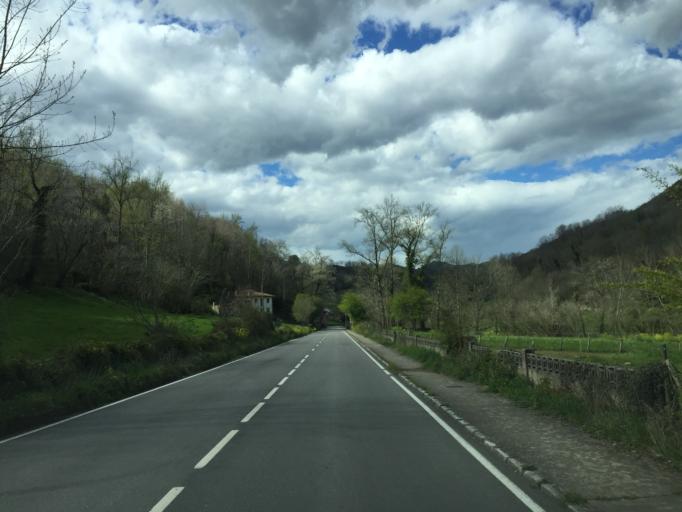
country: ES
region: Asturias
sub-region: Province of Asturias
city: Cangas de Onis
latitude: 43.3208
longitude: -5.0752
